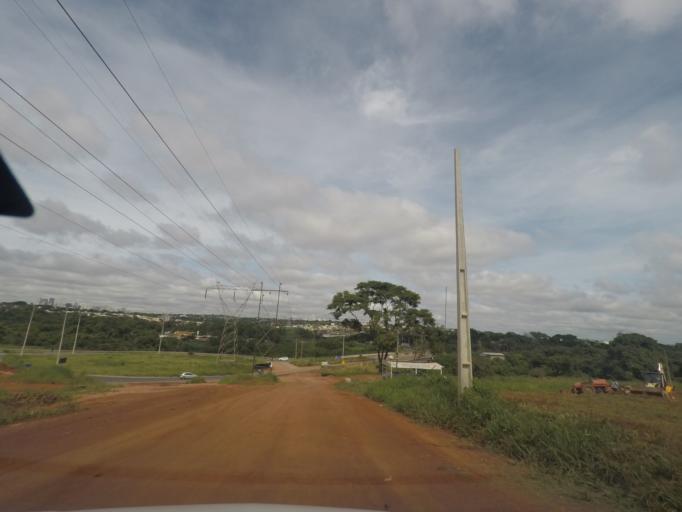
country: BR
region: Goias
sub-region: Goiania
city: Goiania
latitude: -16.6752
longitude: -49.1949
